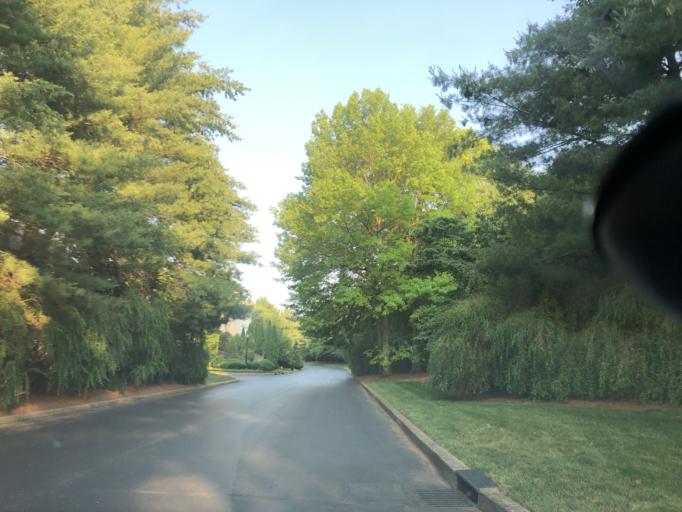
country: US
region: Tennessee
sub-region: Davidson County
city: Belle Meade
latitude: 36.1288
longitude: -86.8252
